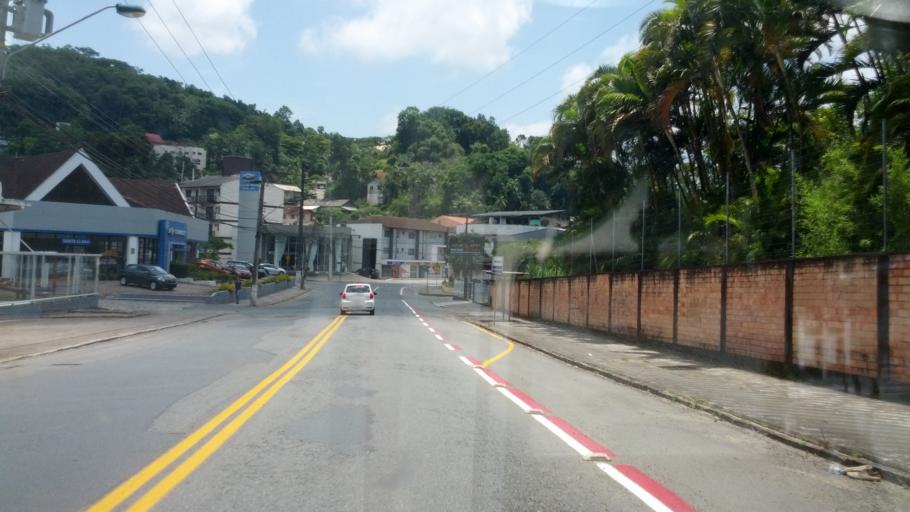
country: BR
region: Santa Catarina
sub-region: Blumenau
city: Blumenau
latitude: -26.8977
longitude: -49.0873
